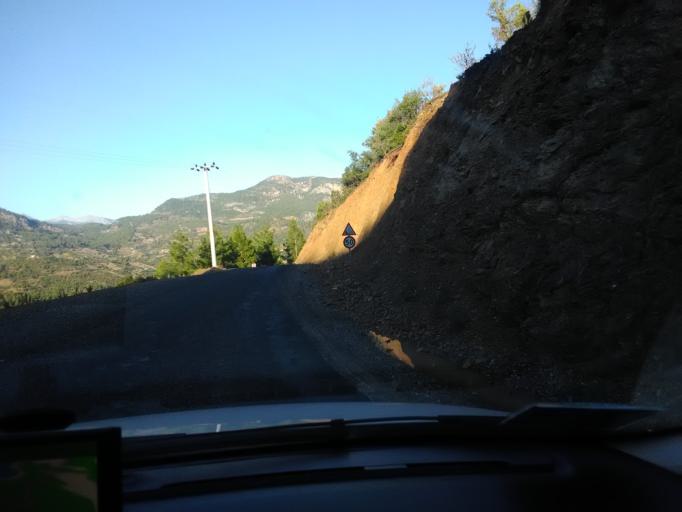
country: TR
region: Antalya
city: Gazipasa
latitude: 36.3042
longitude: 32.4005
